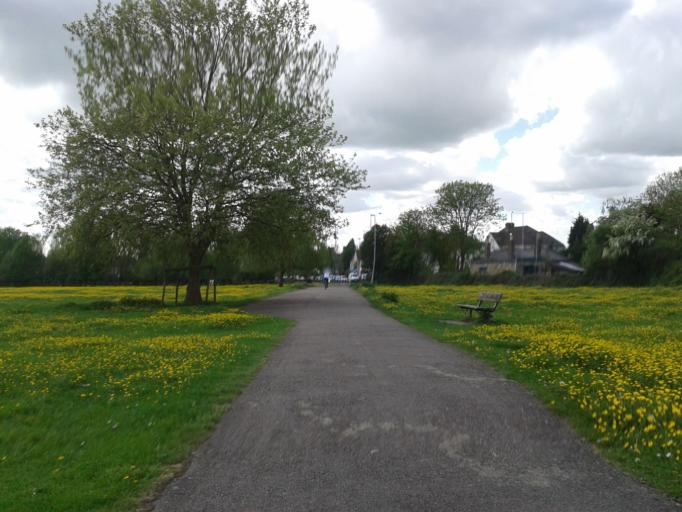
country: GB
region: England
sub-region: Cambridgeshire
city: Cambridge
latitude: 52.2073
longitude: 0.1501
